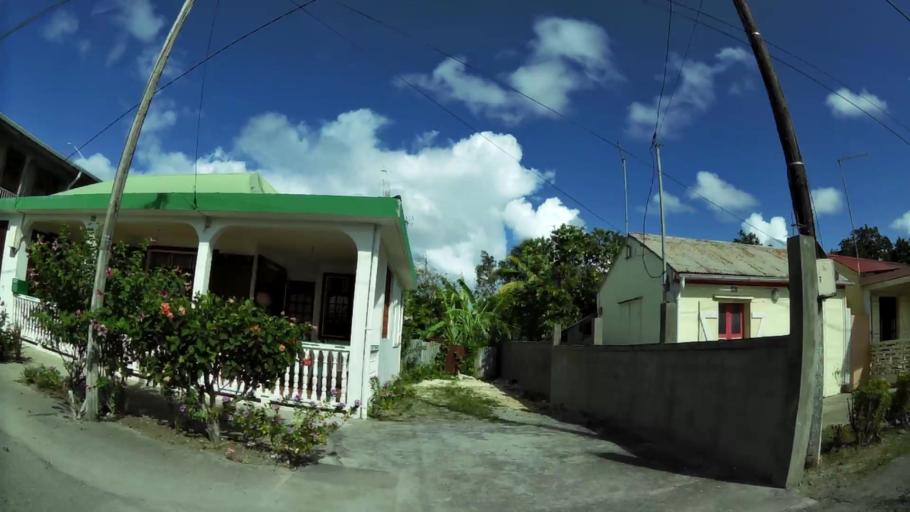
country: GP
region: Guadeloupe
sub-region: Guadeloupe
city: Port-Louis
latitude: 16.4168
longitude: -61.5291
